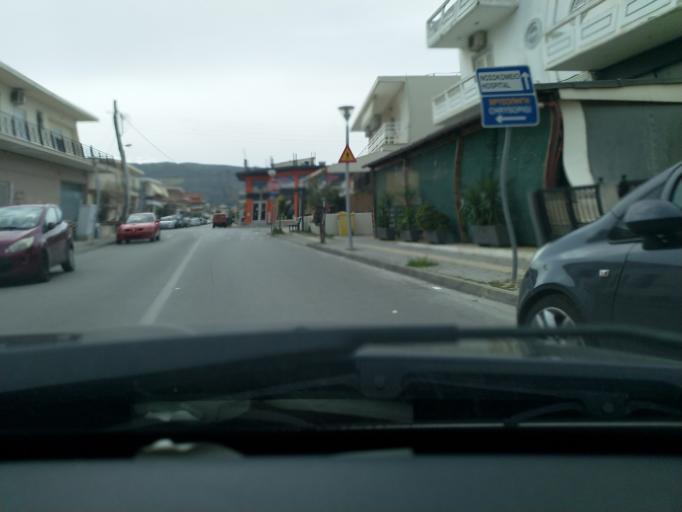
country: GR
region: Crete
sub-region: Nomos Chanias
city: Mournies
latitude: 35.4942
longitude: 24.0227
